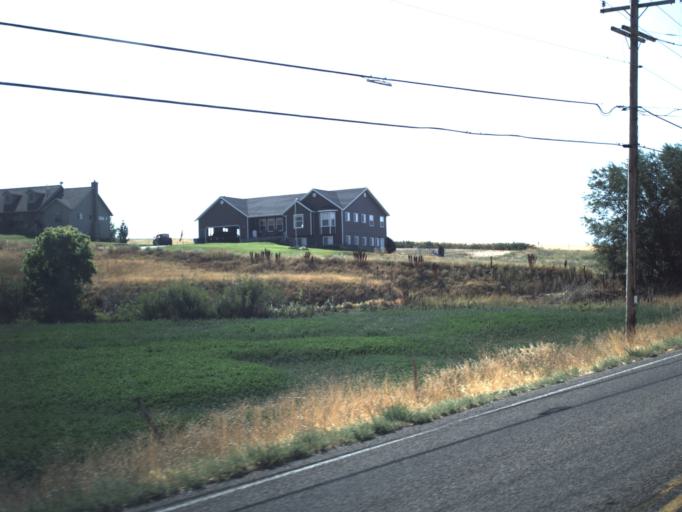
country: US
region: Utah
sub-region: Cache County
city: Hyrum
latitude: 41.5986
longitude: -111.8347
